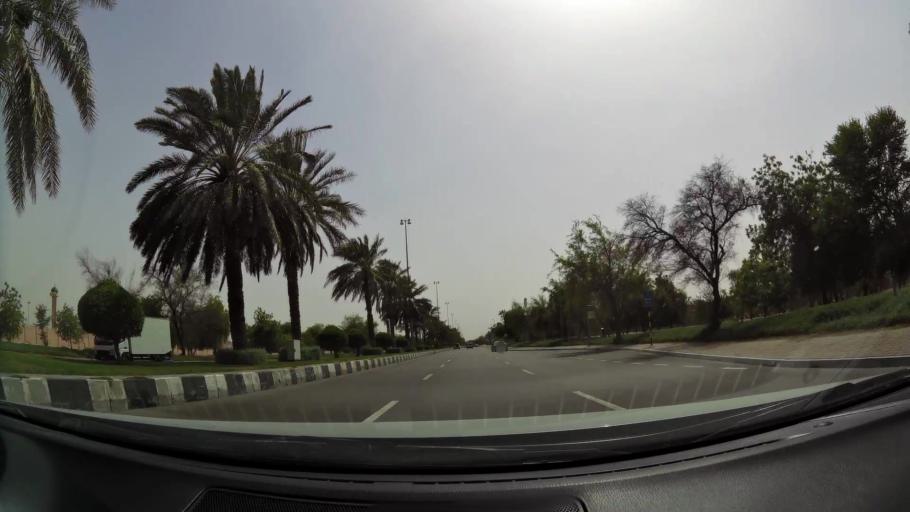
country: AE
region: Abu Dhabi
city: Al Ain
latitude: 24.1915
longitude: 55.6476
